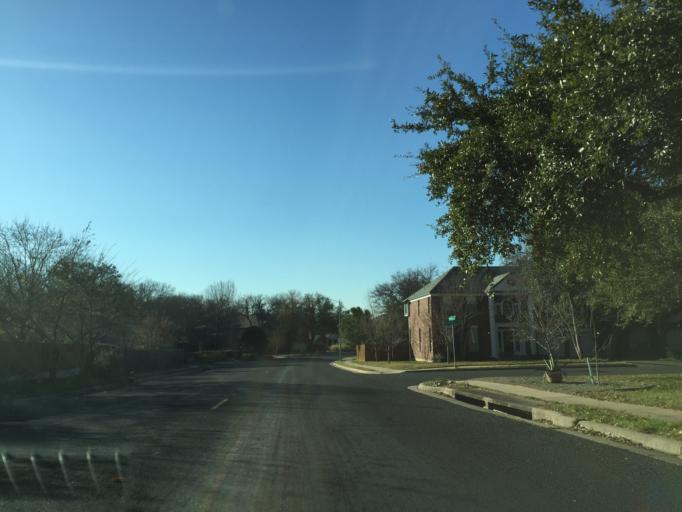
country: US
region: Texas
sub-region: Williamson County
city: Jollyville
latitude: 30.4444
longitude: -97.7644
